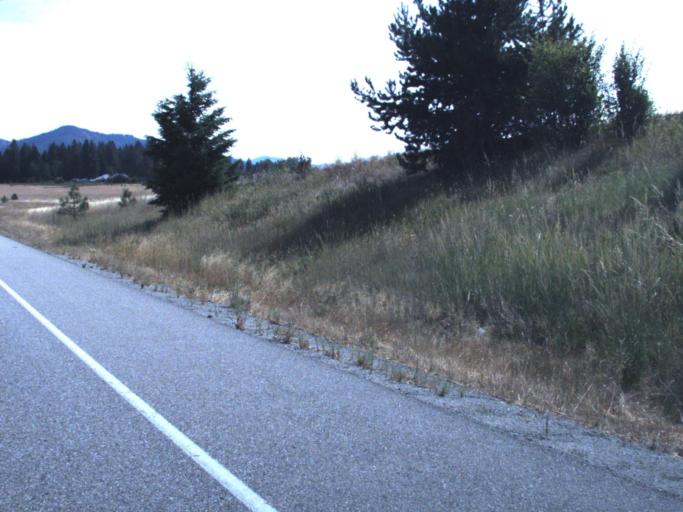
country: US
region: Washington
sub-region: Stevens County
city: Chewelah
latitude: 48.2954
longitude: -117.7473
